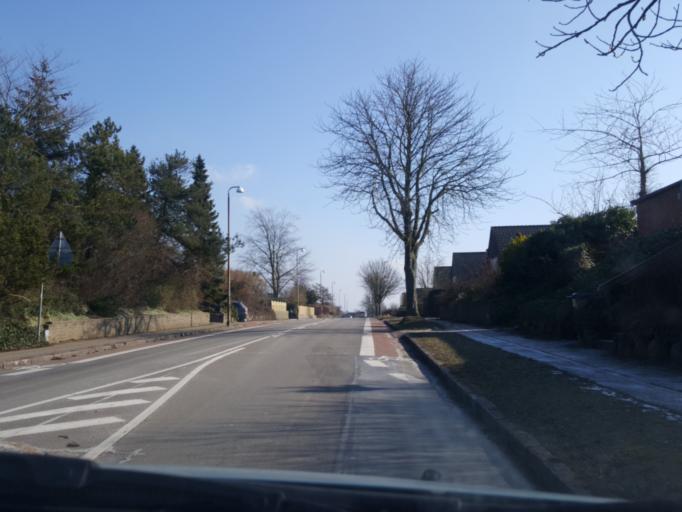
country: DK
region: Zealand
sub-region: Kalundborg Kommune
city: Kalundborg
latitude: 55.6875
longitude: 11.0830
